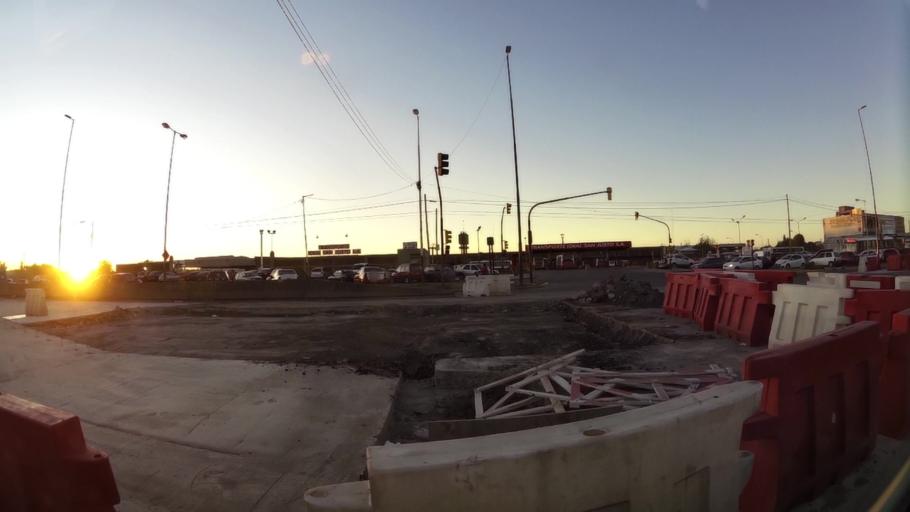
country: AR
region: Buenos Aires
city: Pontevedra
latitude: -34.7451
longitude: -58.6089
